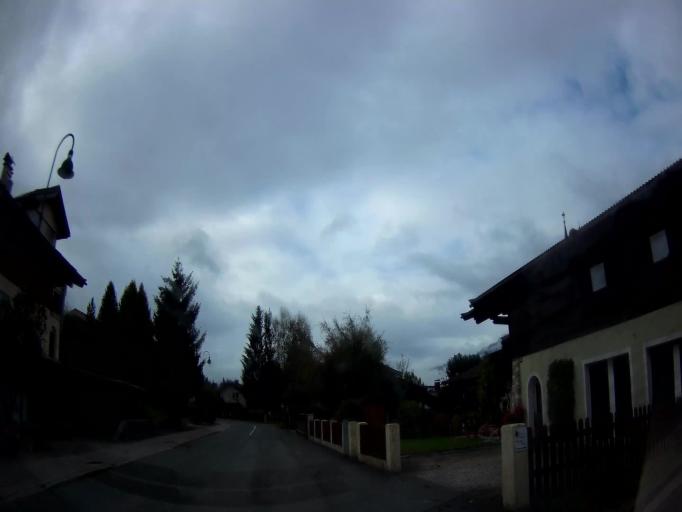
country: AT
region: Salzburg
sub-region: Politischer Bezirk Zell am See
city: Saalfelden am Steinernen Meer
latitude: 47.4230
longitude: 12.8379
